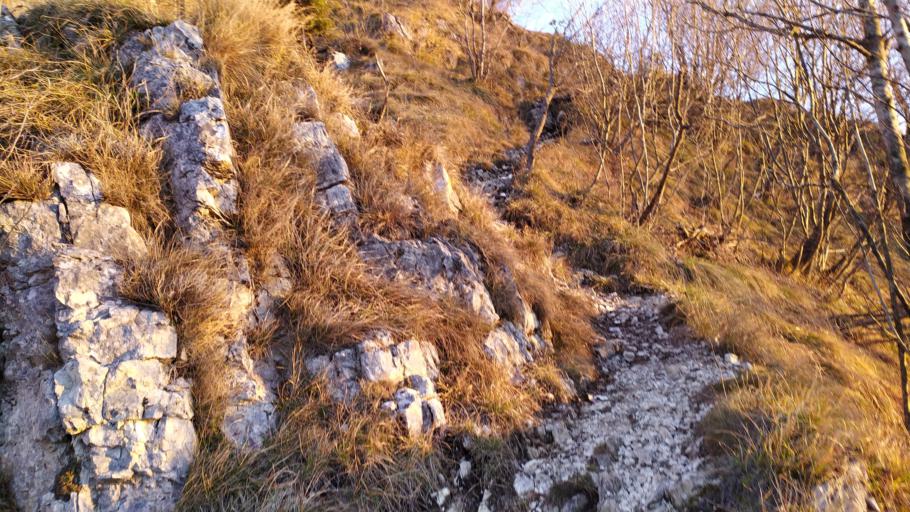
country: IT
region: Veneto
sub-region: Provincia di Vicenza
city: Santorso
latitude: 45.7624
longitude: 11.3821
